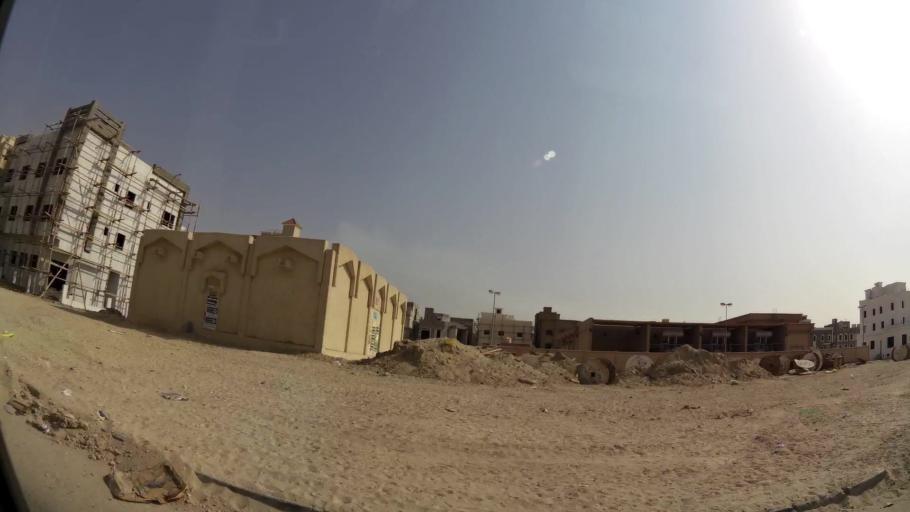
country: KW
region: Muhafazat al Jahra'
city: Al Jahra'
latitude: 29.3546
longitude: 47.7701
